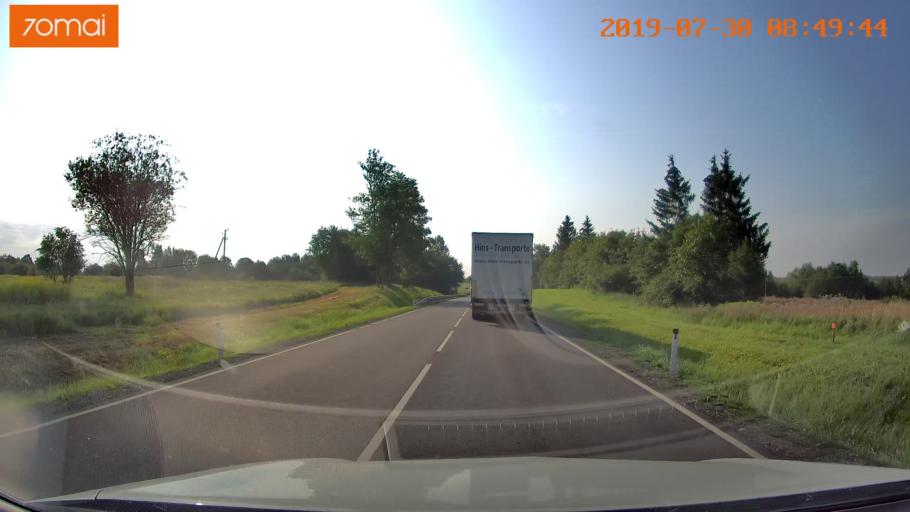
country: RU
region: Kaliningrad
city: Chernyakhovsk
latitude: 54.6115
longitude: 21.9272
